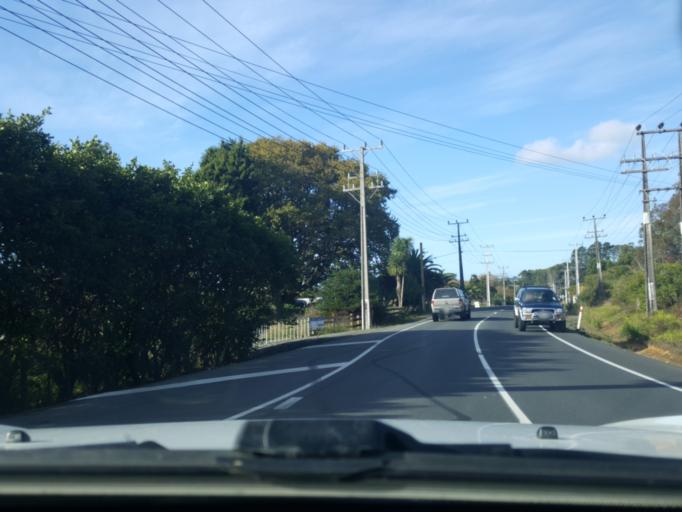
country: NZ
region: Auckland
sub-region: Auckland
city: Muriwai Beach
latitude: -36.7623
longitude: 174.5776
